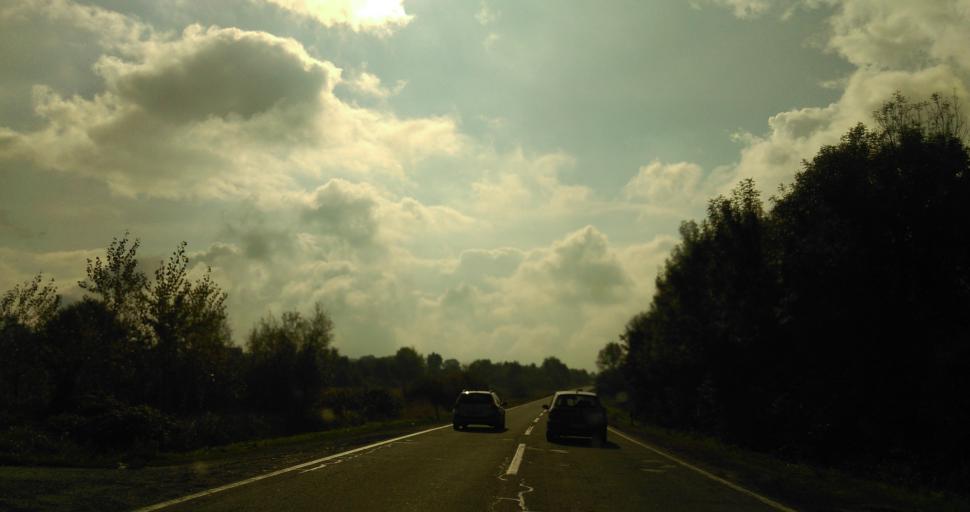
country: RS
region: Central Serbia
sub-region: Kolubarski Okrug
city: Ljig
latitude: 44.2811
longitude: 20.2779
